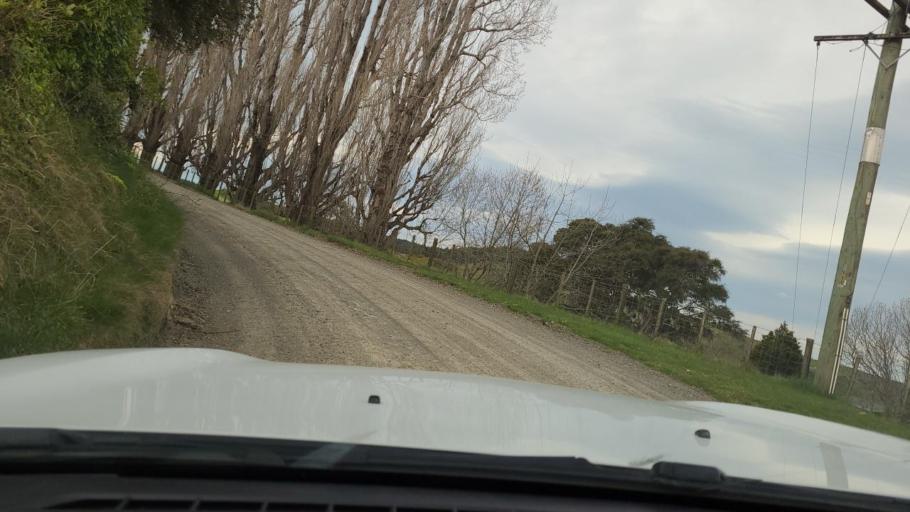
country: NZ
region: Hawke's Bay
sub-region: Napier City
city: Napier
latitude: -39.3002
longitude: 176.8335
